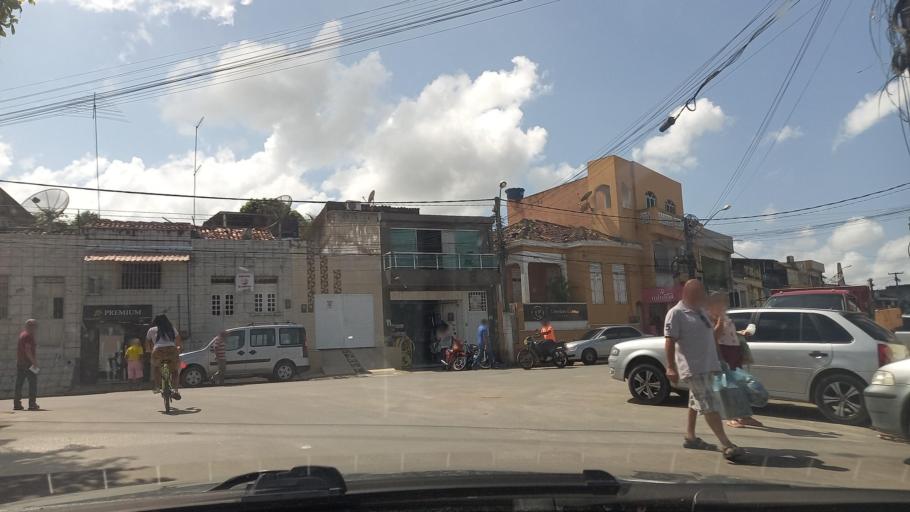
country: BR
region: Pernambuco
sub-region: Goiana
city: Goiana
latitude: -7.5619
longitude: -35.0017
